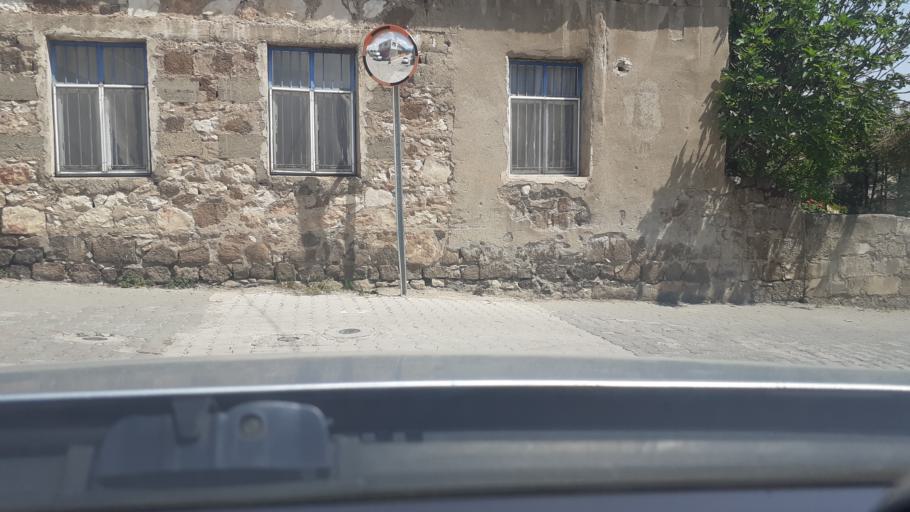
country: TR
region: Hatay
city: Kirikhan
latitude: 36.5020
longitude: 36.3591
